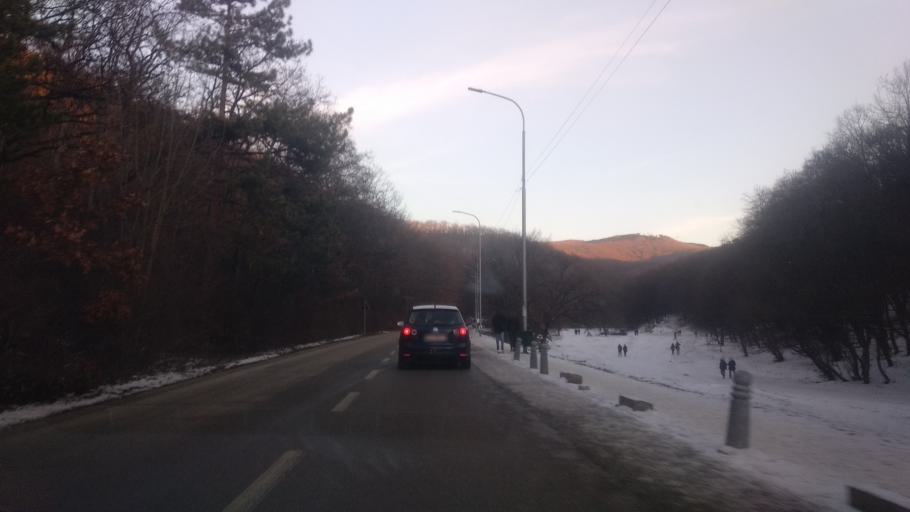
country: XK
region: Pristina
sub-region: Komuna e Prishtines
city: Pristina
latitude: 42.6762
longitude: 21.2092
